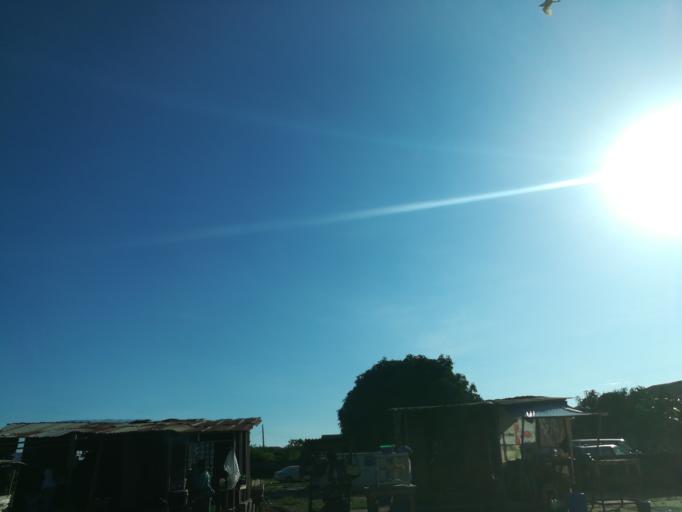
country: NG
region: Lagos
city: Ebute Ikorodu
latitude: 6.5447
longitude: 3.5442
